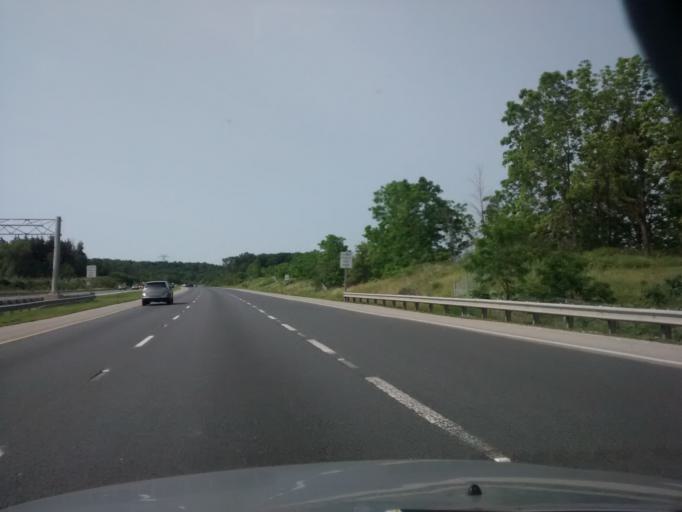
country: CA
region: Ontario
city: Hamilton
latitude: 43.2156
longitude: -79.8021
